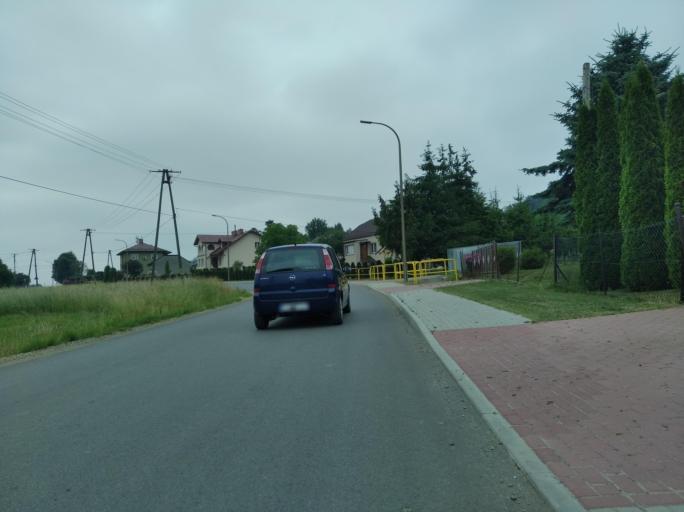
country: PL
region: Subcarpathian Voivodeship
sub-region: Powiat krosnienski
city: Rymanow
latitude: 49.6022
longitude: 21.9026
